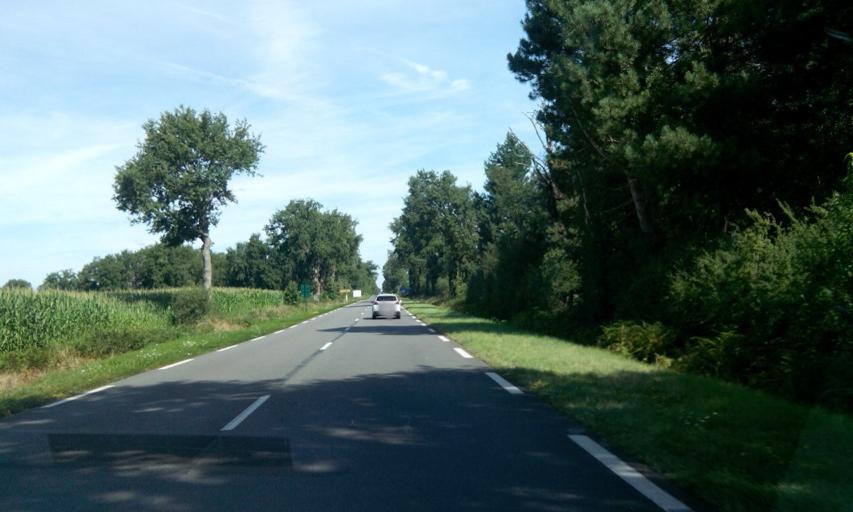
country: FR
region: Poitou-Charentes
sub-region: Departement de la Vienne
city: Availles-Limouzine
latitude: 46.0789
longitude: 0.5902
